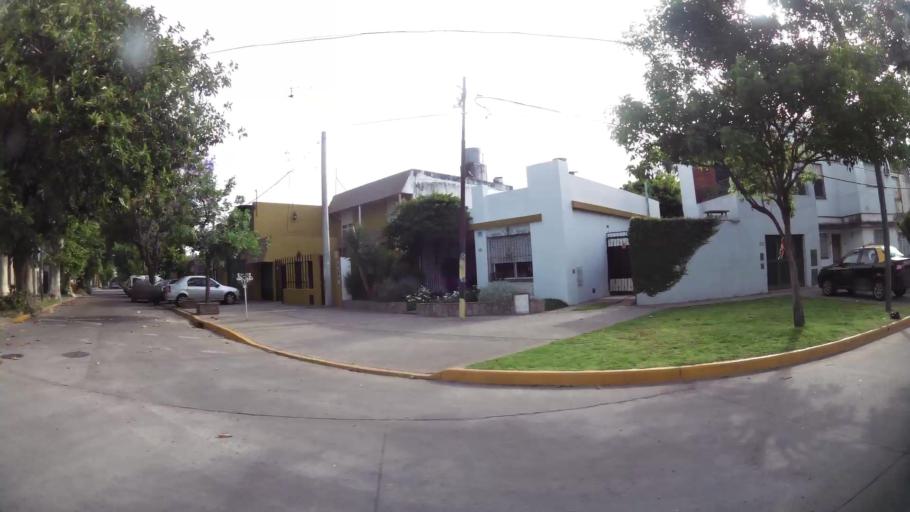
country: AR
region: Santa Fe
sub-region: Departamento de Rosario
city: Rosario
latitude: -32.9274
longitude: -60.6790
